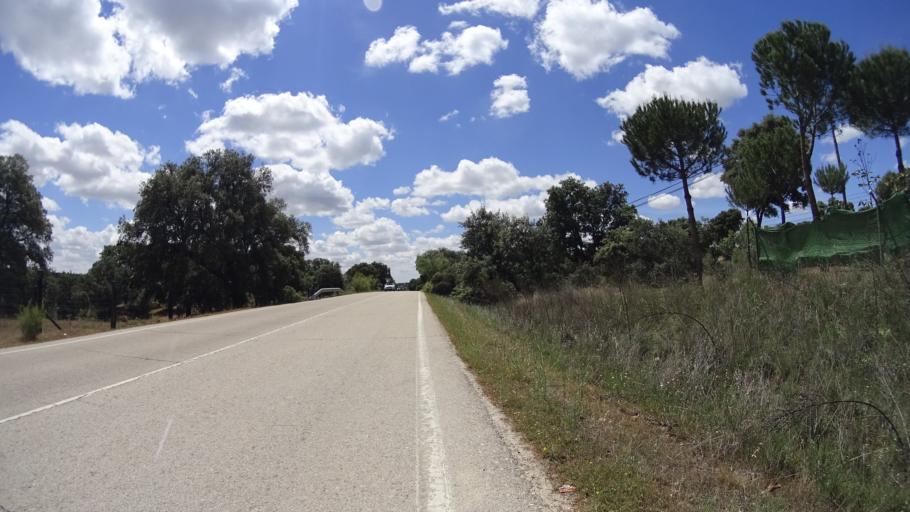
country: ES
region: Madrid
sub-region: Provincia de Madrid
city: Villanueva del Pardillo
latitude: 40.4489
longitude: -3.9534
